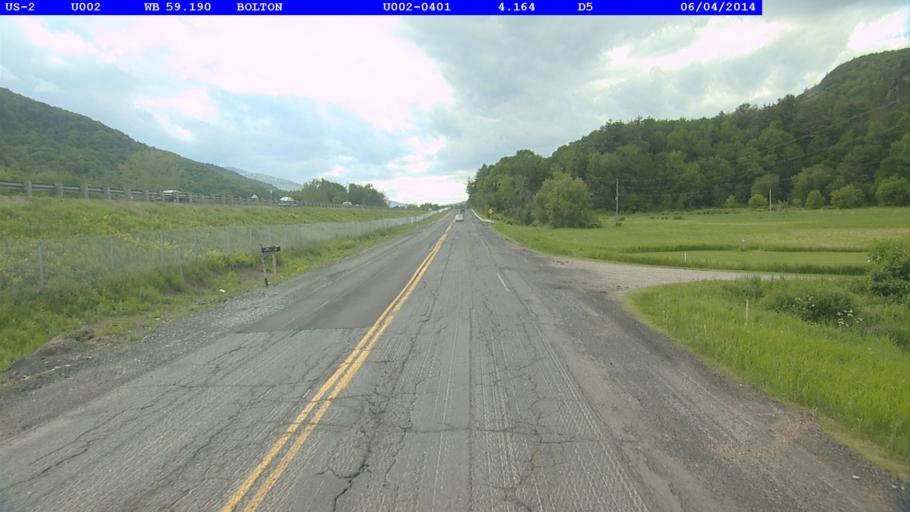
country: US
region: Vermont
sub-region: Washington County
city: Waterbury
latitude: 44.3664
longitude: -72.8535
